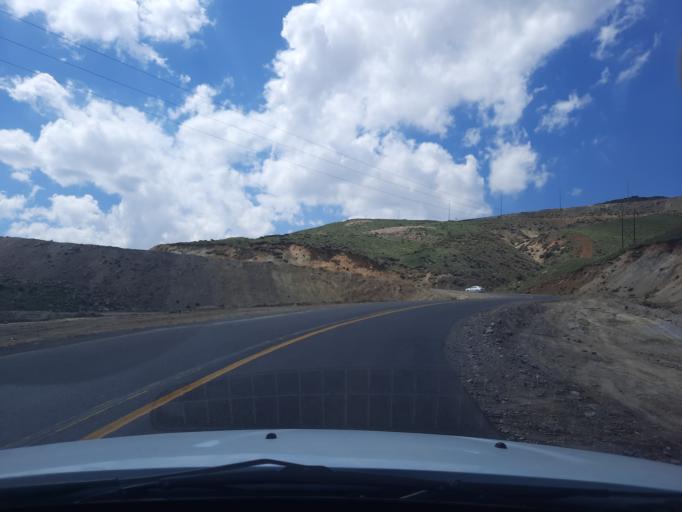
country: IR
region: Qazvin
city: Qazvin
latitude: 36.3816
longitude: 50.2077
